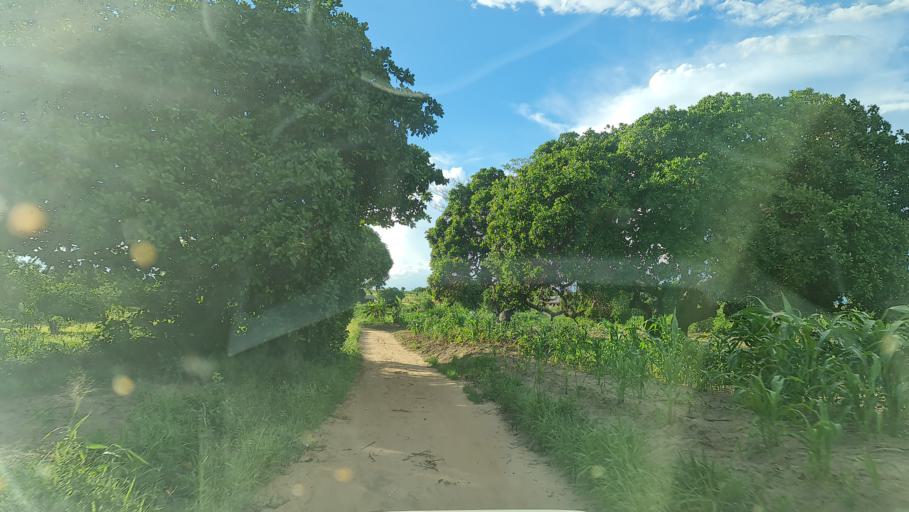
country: MZ
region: Nampula
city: Ilha de Mocambique
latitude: -14.9438
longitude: 40.1667
